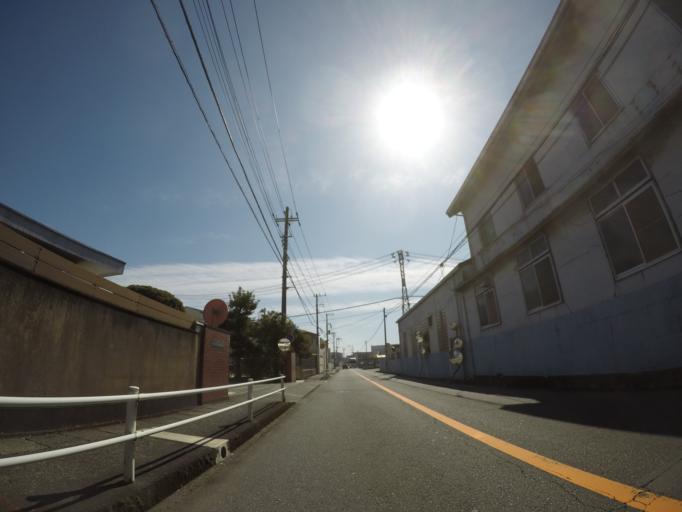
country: JP
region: Shizuoka
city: Fuji
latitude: 35.1604
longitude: 138.6960
